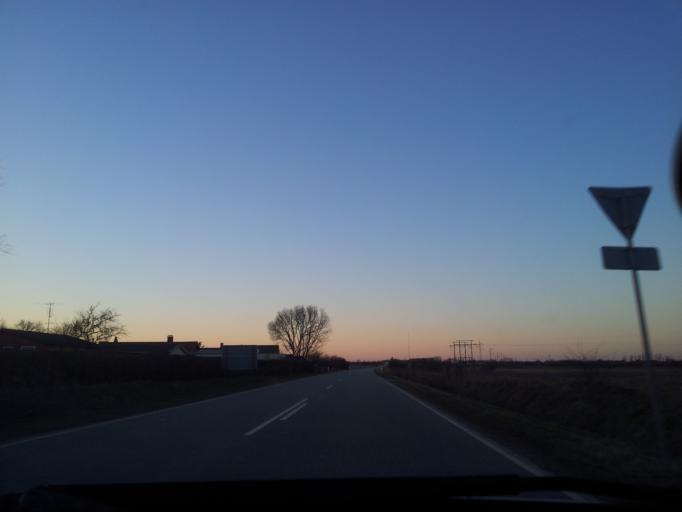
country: DE
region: Schleswig-Holstein
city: Rodenas
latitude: 54.9649
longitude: 8.7026
